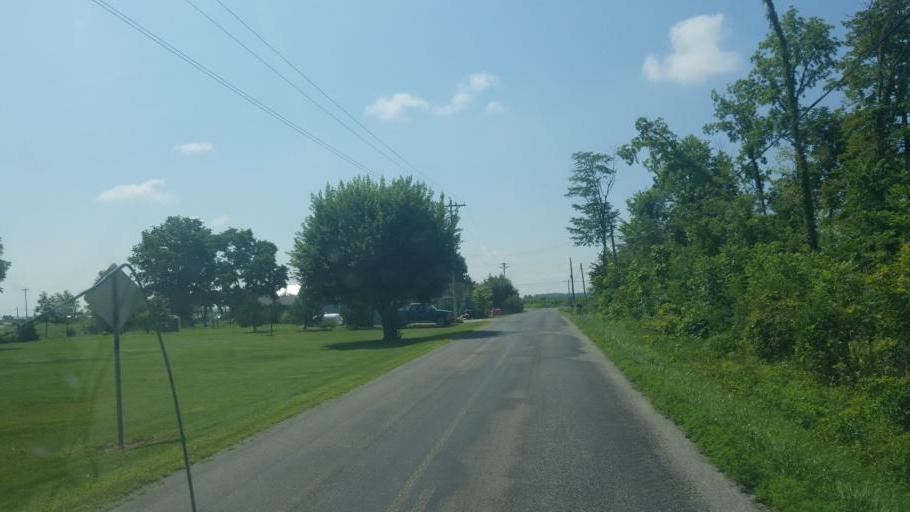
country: US
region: Ohio
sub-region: Hardin County
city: Ada
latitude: 40.6756
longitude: -83.7410
